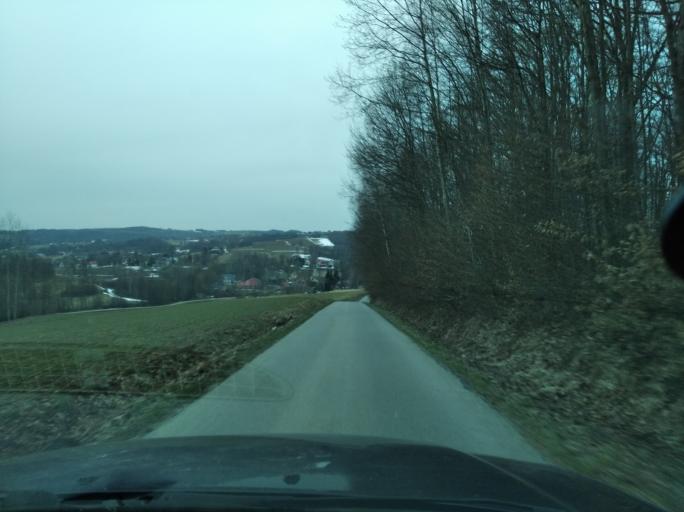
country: PL
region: Subcarpathian Voivodeship
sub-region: Powiat rzeszowski
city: Chmielnik
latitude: 49.9816
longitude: 22.1350
